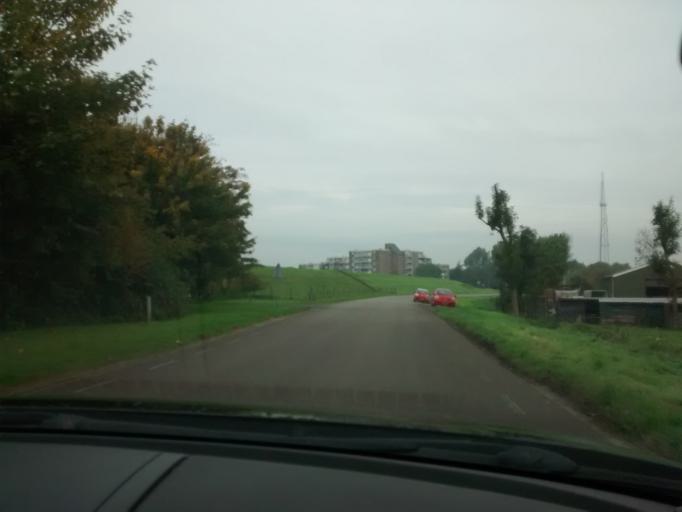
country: NL
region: South Holland
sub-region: Gemeente Hellevoetsluis
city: Hellevoetsluis
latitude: 51.8222
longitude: 4.1620
